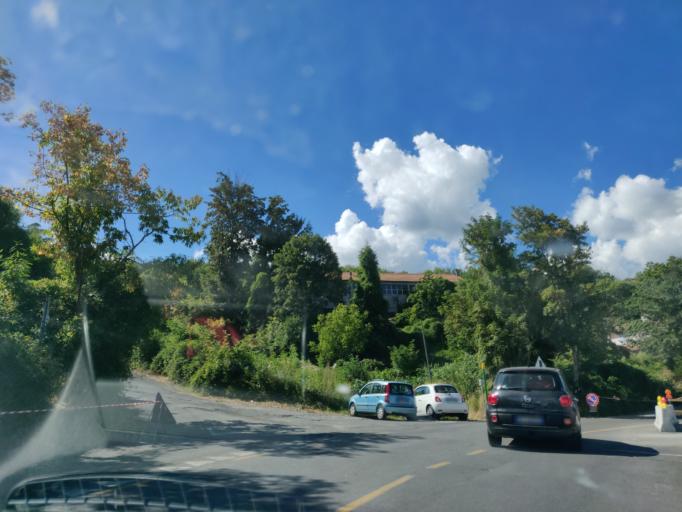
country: IT
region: Tuscany
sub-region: Provincia di Siena
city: Abbadia San Salvatore
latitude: 42.8892
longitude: 11.6662
